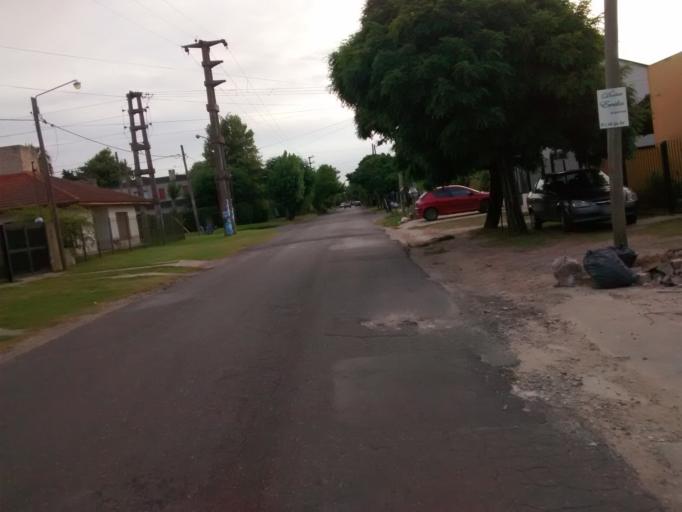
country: AR
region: Buenos Aires
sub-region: Partido de La Plata
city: La Plata
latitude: -34.8697
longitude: -58.0563
